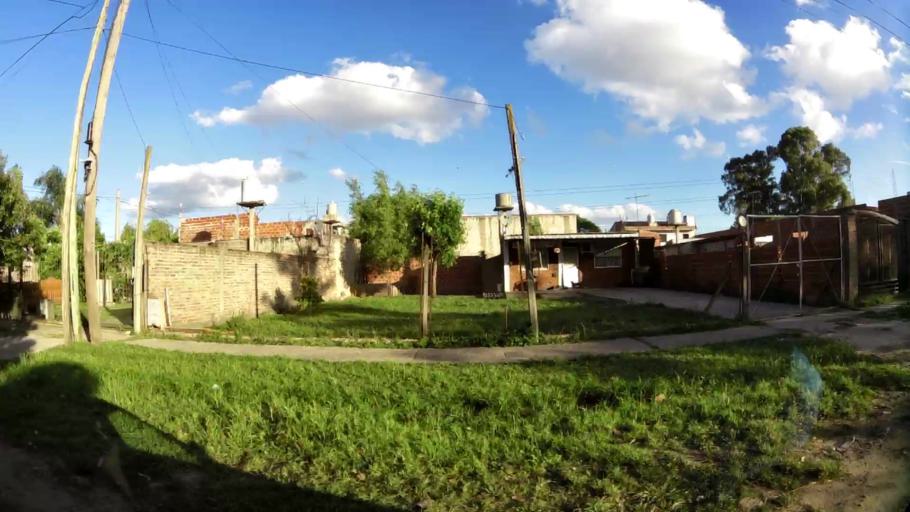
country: AR
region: Buenos Aires
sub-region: Partido de Moron
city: Moron
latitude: -34.7095
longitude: -58.6177
